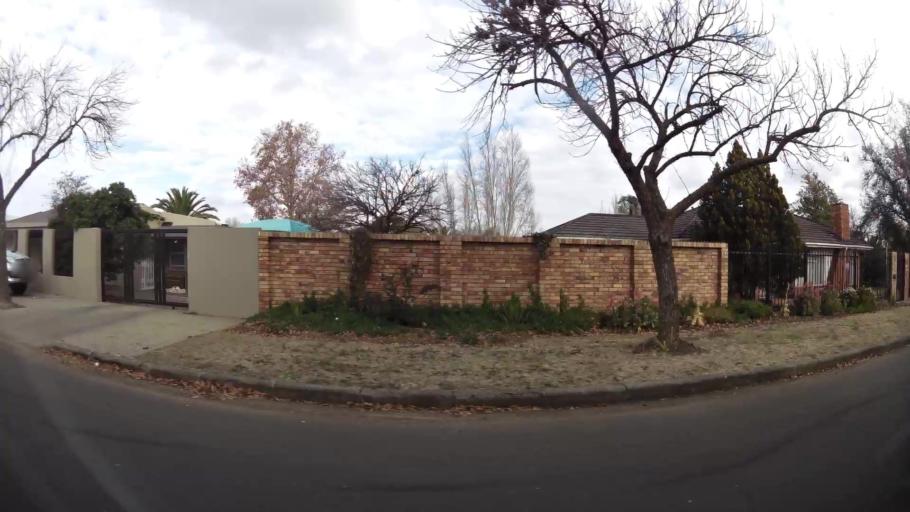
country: ZA
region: Orange Free State
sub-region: Mangaung Metropolitan Municipality
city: Bloemfontein
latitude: -29.0830
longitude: 26.2086
